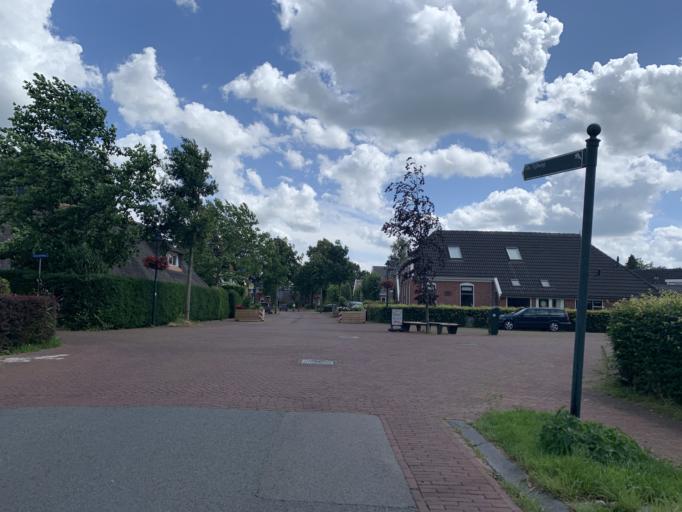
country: NL
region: Groningen
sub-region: Gemeente Haren
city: Haren
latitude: 53.1586
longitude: 6.6400
